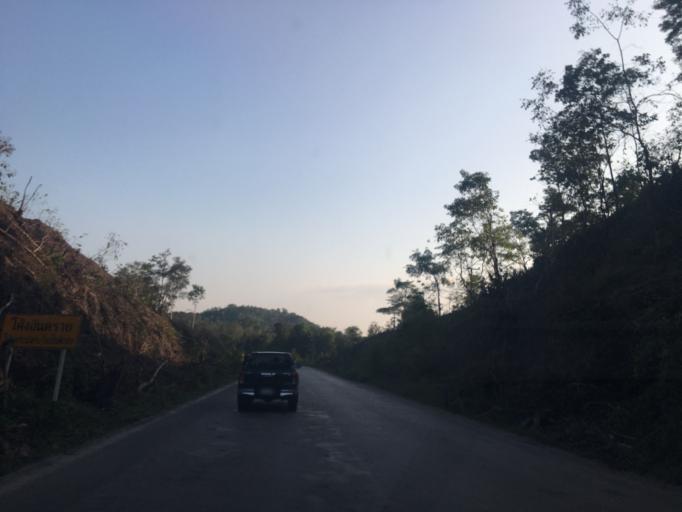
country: TH
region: Lampang
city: Ngao
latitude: 18.6267
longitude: 100.0182
